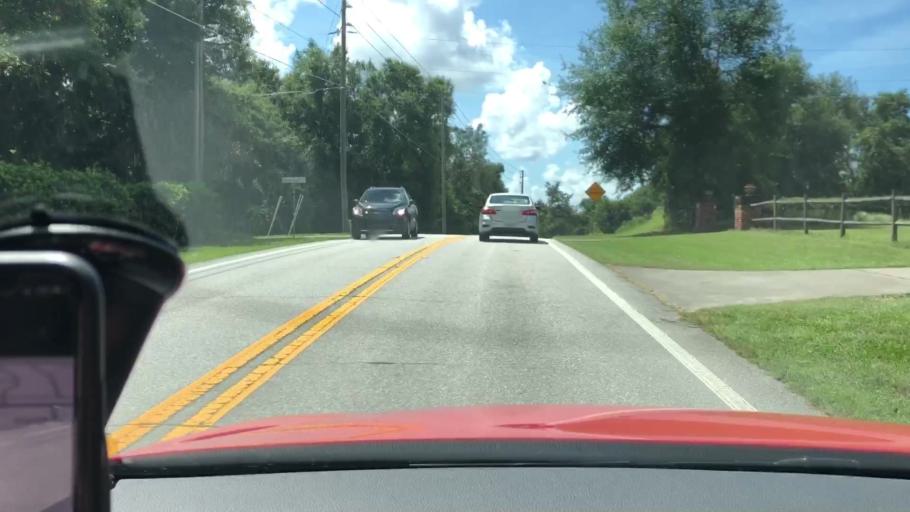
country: US
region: Florida
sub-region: Lake County
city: Eustis
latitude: 28.8406
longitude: -81.6545
